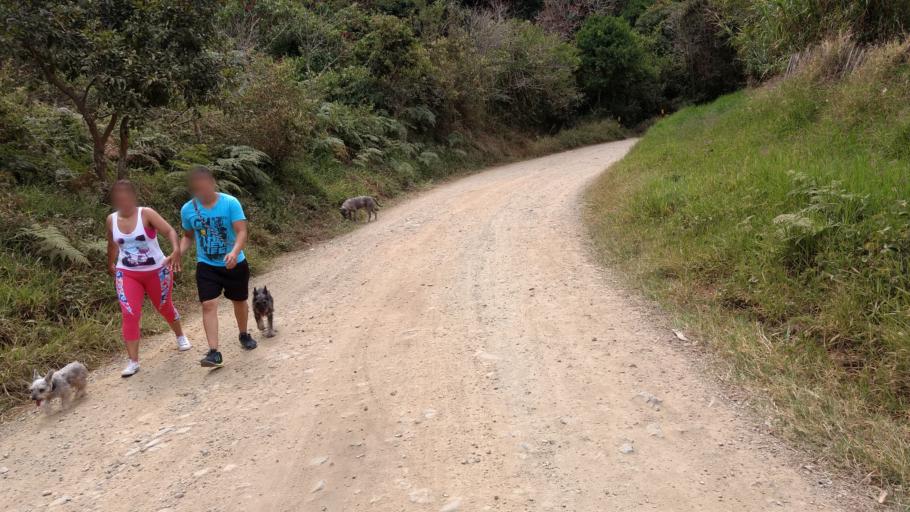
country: CO
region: Cauca
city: Popayan
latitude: 2.4662
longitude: -76.5757
